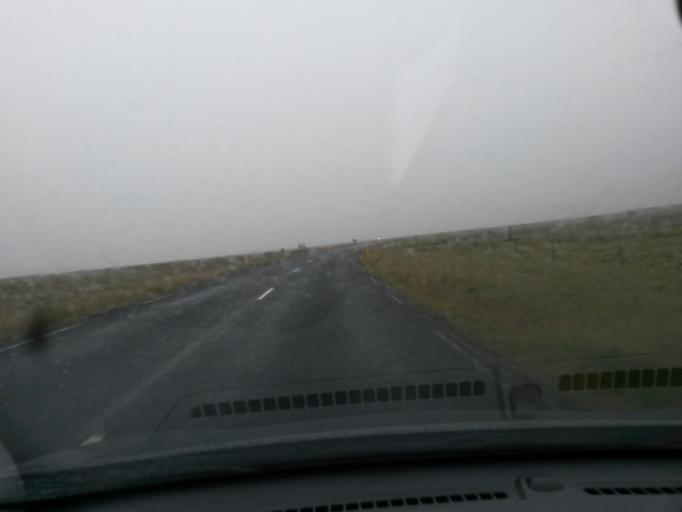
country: IS
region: South
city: Vestmannaeyjar
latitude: 63.4342
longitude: -19.1910
